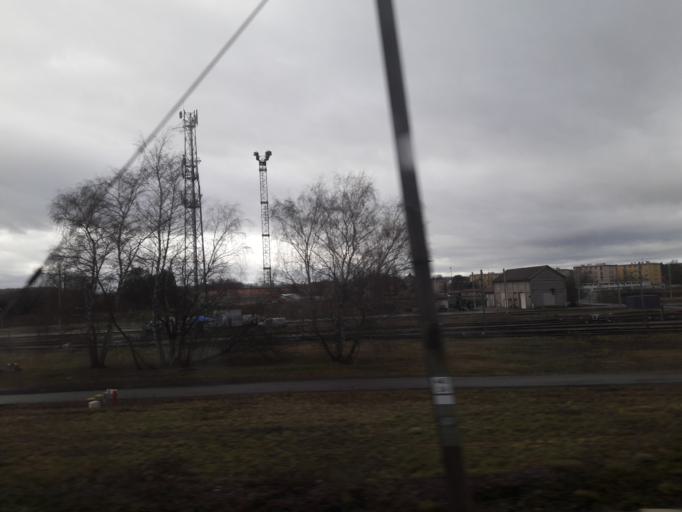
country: FR
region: Franche-Comte
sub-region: Territoire de Belfort
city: Belfort
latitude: 47.6256
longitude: 6.8580
